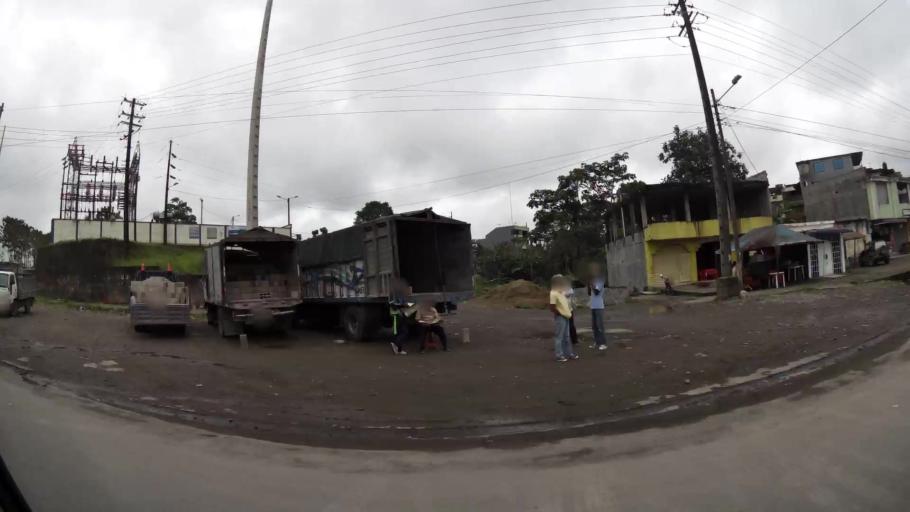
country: EC
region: Santo Domingo de los Tsachilas
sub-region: Canton Santo Domingo de los Colorados
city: Santo Domingo de los Colorados
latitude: -0.2329
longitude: -79.1660
